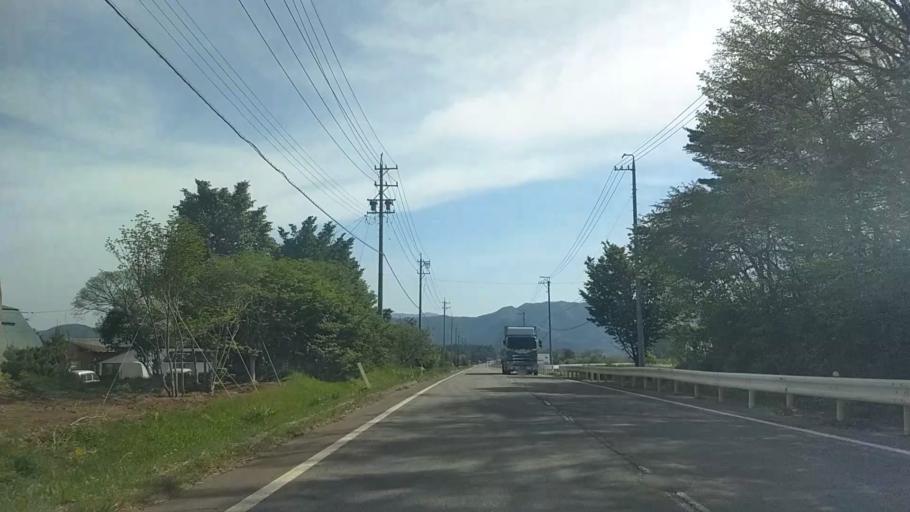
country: JP
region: Nagano
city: Saku
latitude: 35.9910
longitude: 138.4906
